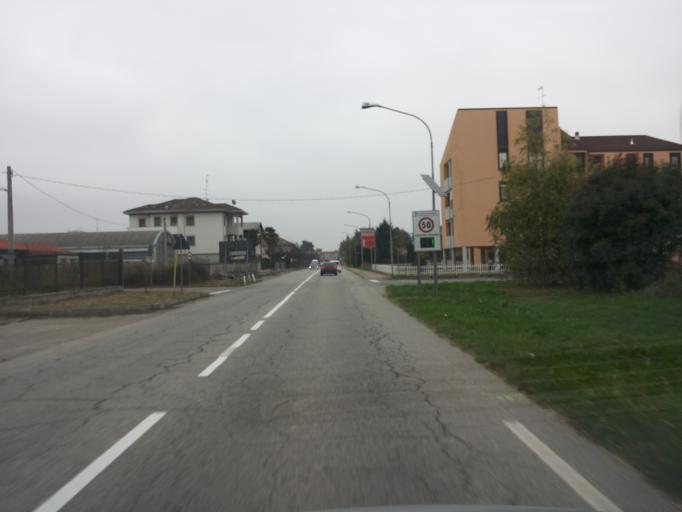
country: IT
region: Piedmont
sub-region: Provincia di Vercelli
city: Borgo Vercelli
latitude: 45.3529
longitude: 8.4608
